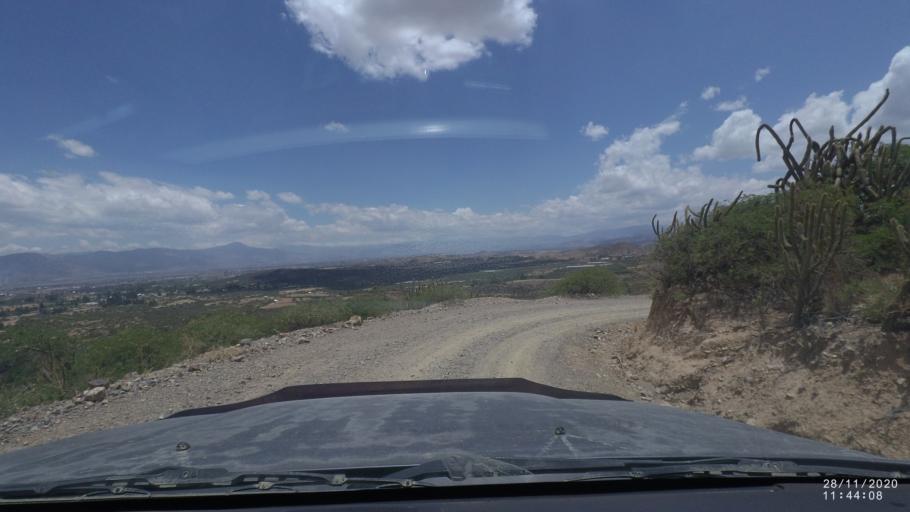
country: BO
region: Cochabamba
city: Tarata
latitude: -17.6606
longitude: -66.0440
